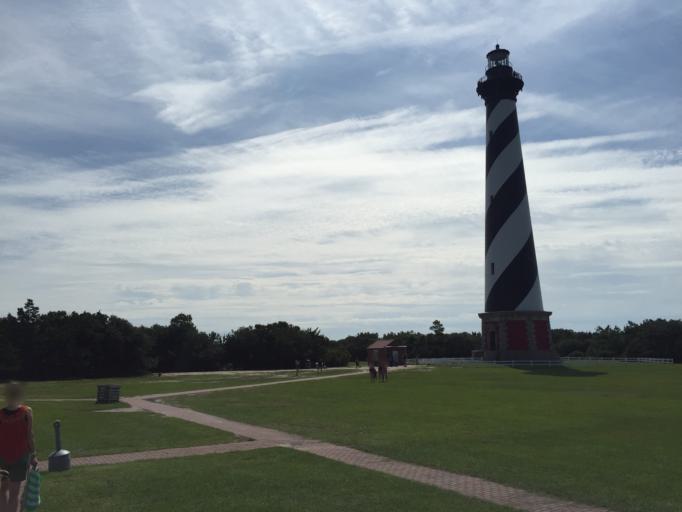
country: US
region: North Carolina
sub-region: Dare County
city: Buxton
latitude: 35.2512
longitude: -75.5297
